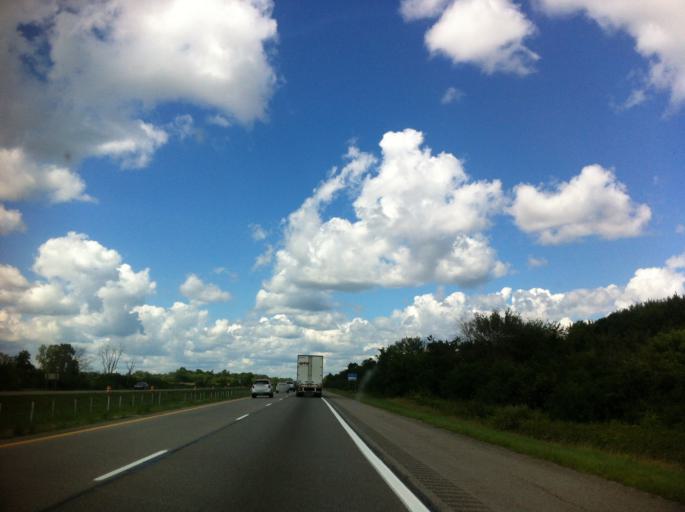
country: US
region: Michigan
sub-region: Washtenaw County
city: Ypsilanti
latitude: 42.1904
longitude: -83.6845
